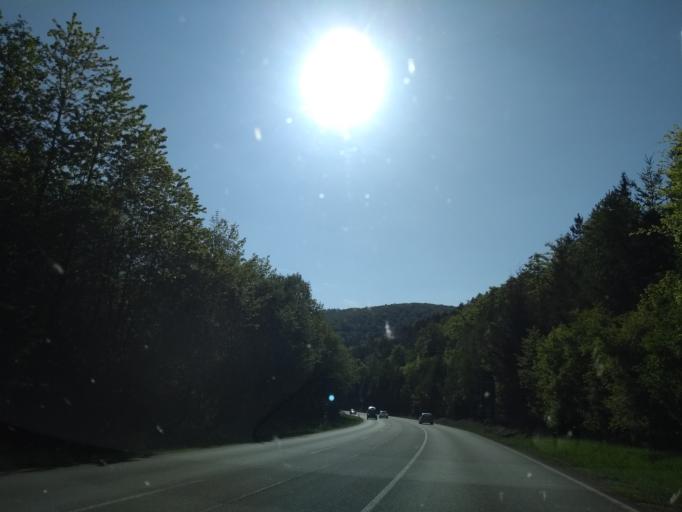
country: DE
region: Hesse
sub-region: Regierungsbezirk Giessen
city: Biedenkopf
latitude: 50.9406
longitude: 8.5452
